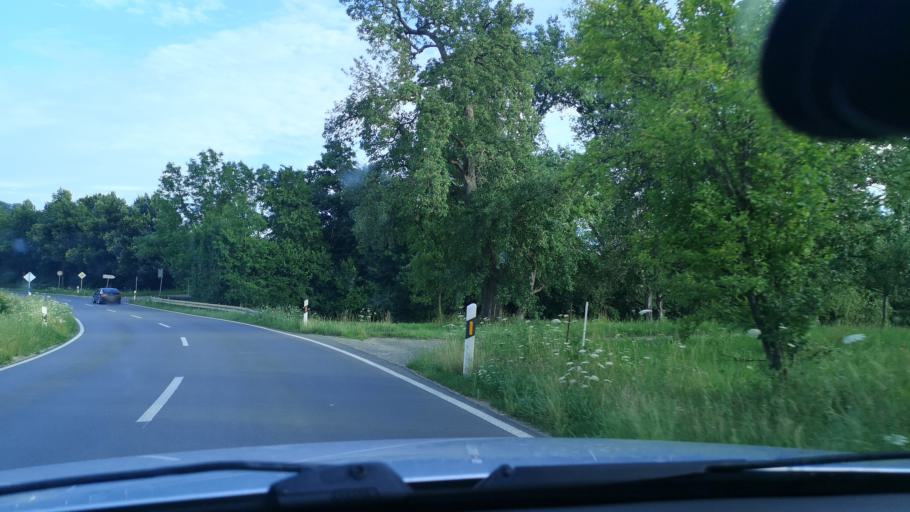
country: DE
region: Baden-Wuerttemberg
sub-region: Regierungsbezirk Stuttgart
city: Boll
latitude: 48.6713
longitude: 9.6118
